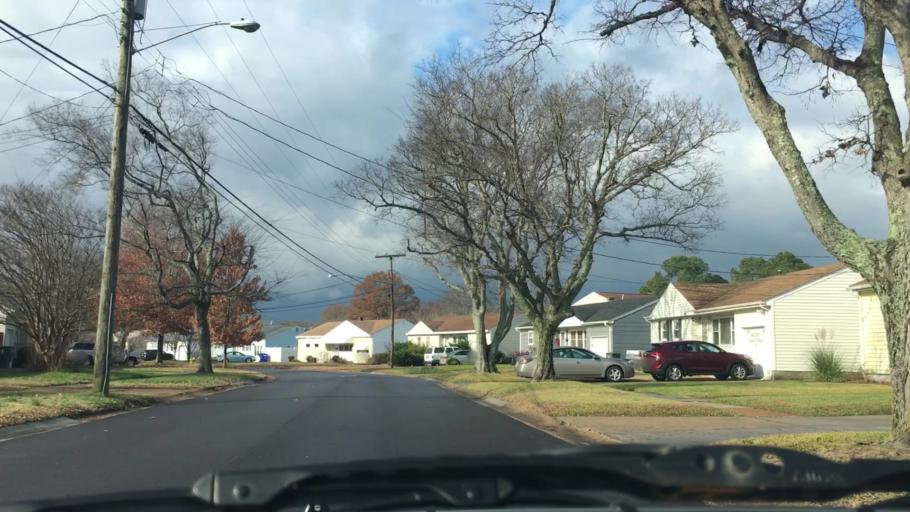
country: US
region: Virginia
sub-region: City of Norfolk
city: Norfolk
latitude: 36.9288
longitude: -76.2321
